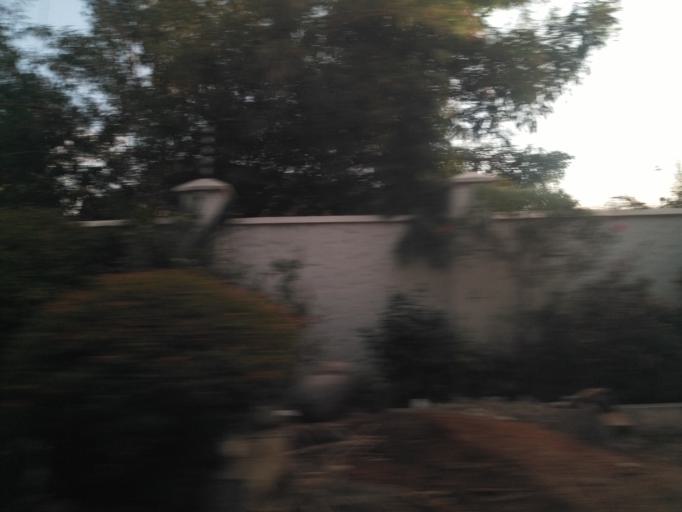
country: TZ
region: Dar es Salaam
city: Magomeni
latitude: -6.7817
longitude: 39.2727
